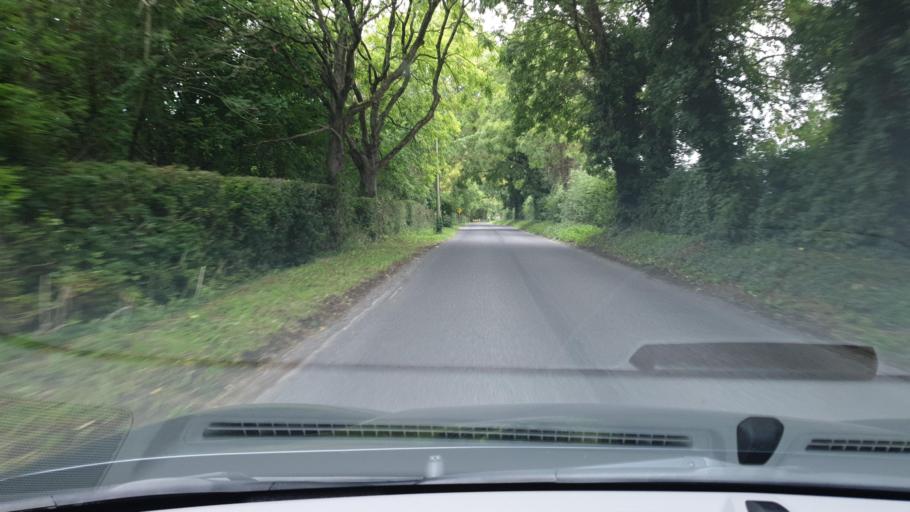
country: IE
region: Leinster
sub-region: Kildare
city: Maynooth
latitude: 53.3711
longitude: -6.6314
